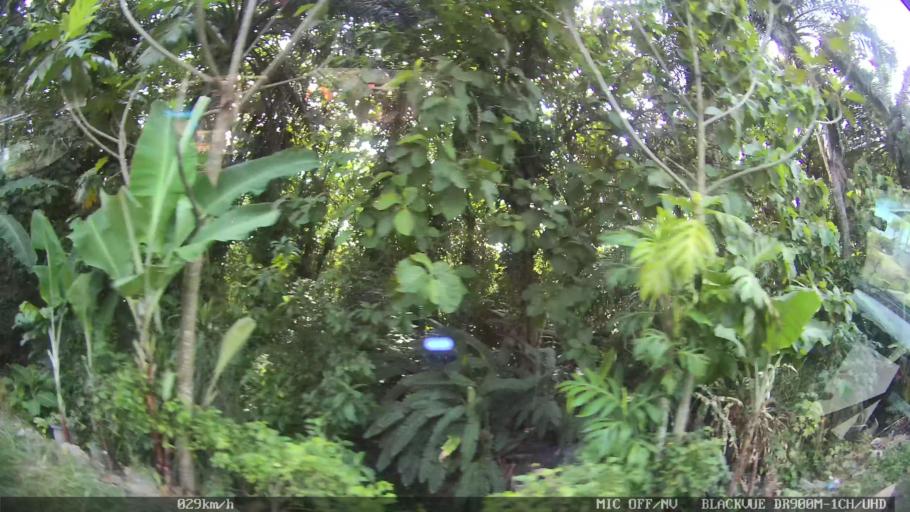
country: ID
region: North Sumatra
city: Binjai
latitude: 3.6484
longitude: 98.5178
